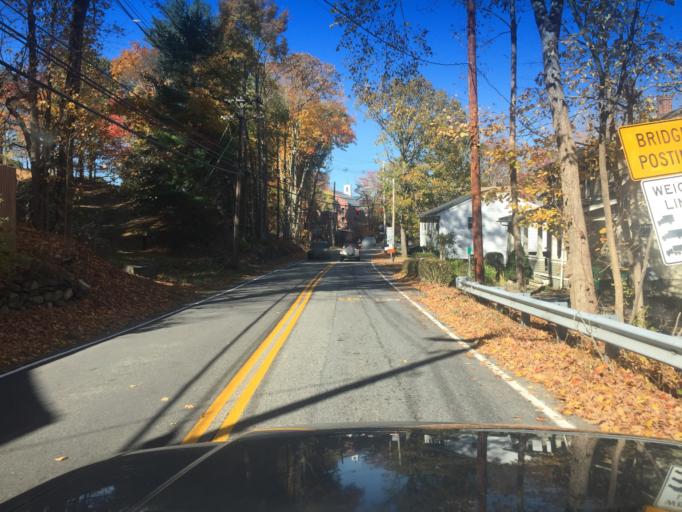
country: US
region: Massachusetts
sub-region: Middlesex County
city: Stow
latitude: 42.4033
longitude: -71.5265
